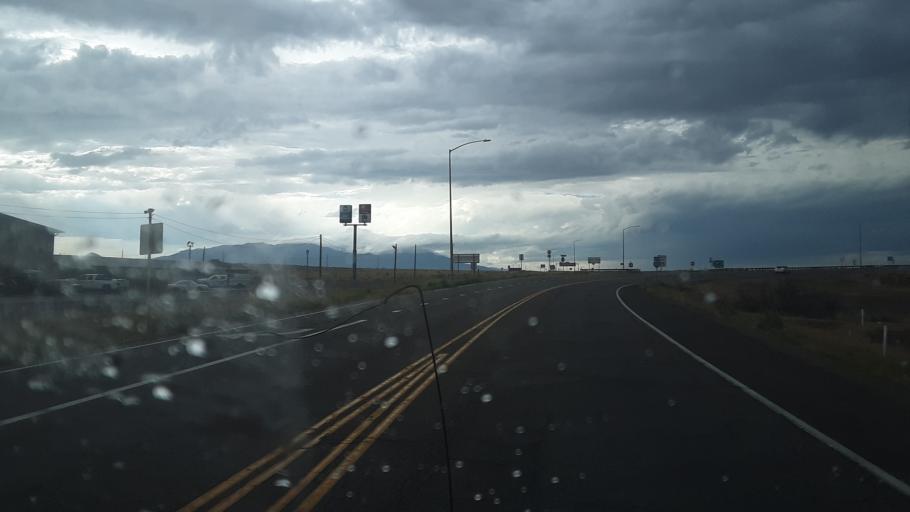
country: US
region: Colorado
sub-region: Huerfano County
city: Walsenburg
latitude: 37.6549
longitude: -104.7936
